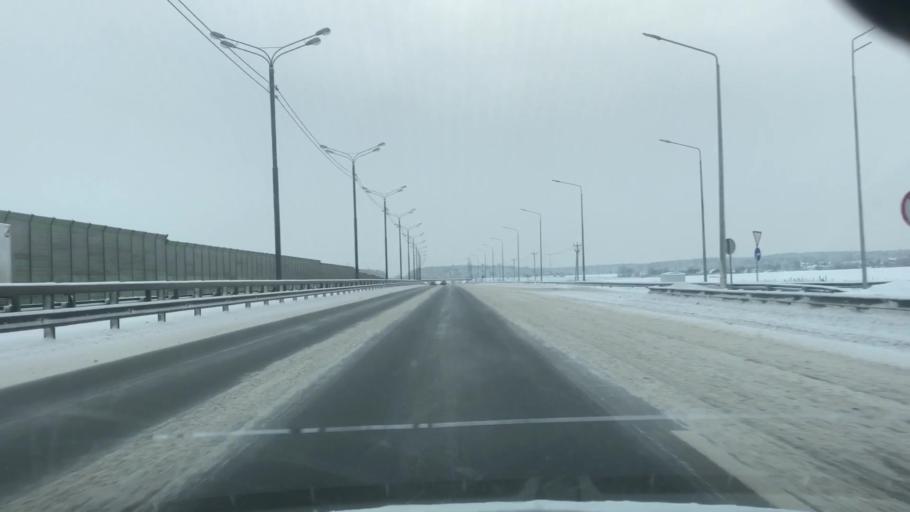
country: RU
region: Moskovskaya
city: Barybino
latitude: 55.1924
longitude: 37.8941
